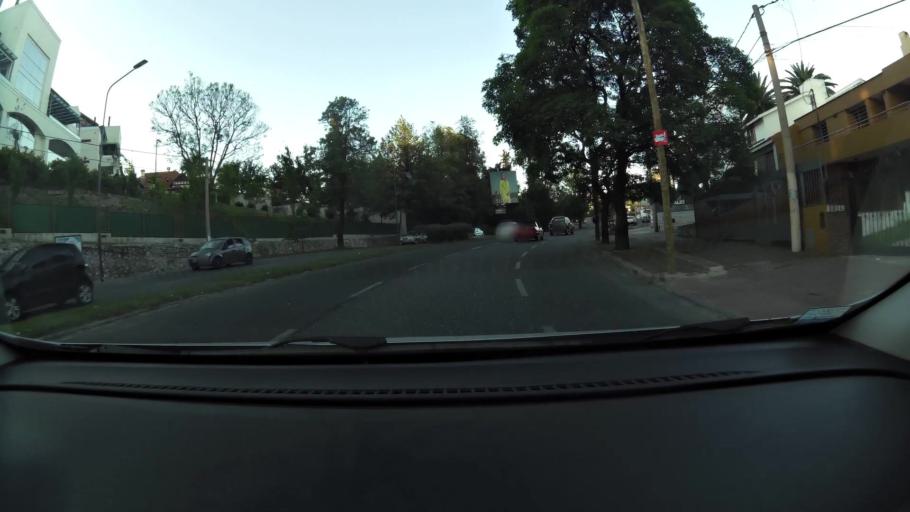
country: AR
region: Cordoba
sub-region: Departamento de Capital
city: Cordoba
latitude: -31.3818
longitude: -64.2237
